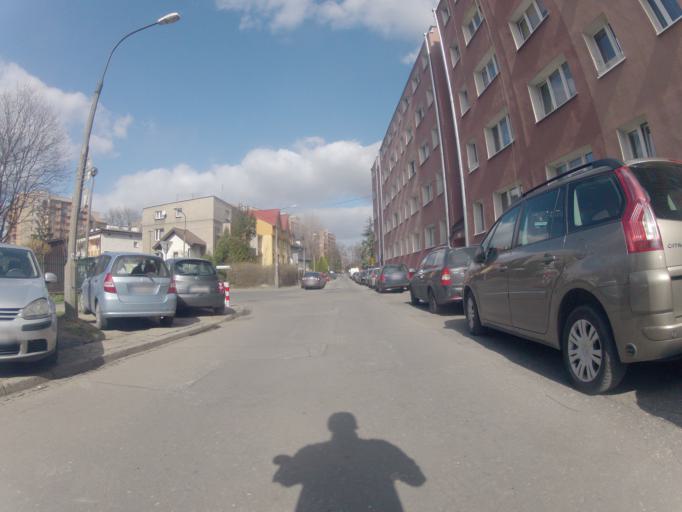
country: PL
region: Lesser Poland Voivodeship
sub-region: Krakow
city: Krakow
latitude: 50.0823
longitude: 19.9549
